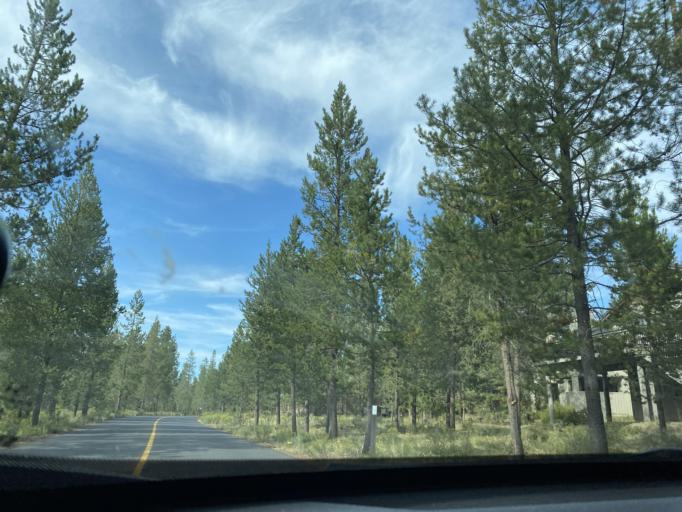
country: US
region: Oregon
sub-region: Deschutes County
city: Sunriver
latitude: 43.8922
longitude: -121.4387
